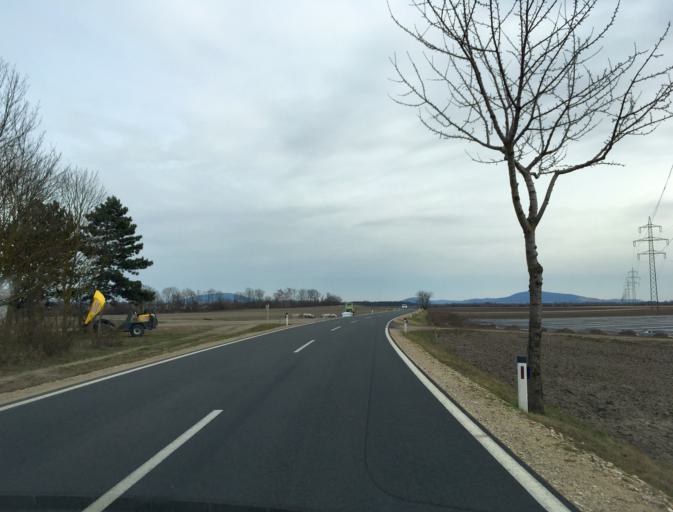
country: AT
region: Lower Austria
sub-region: Politischer Bezirk Ganserndorf
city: Lassee
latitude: 48.2226
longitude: 16.7993
